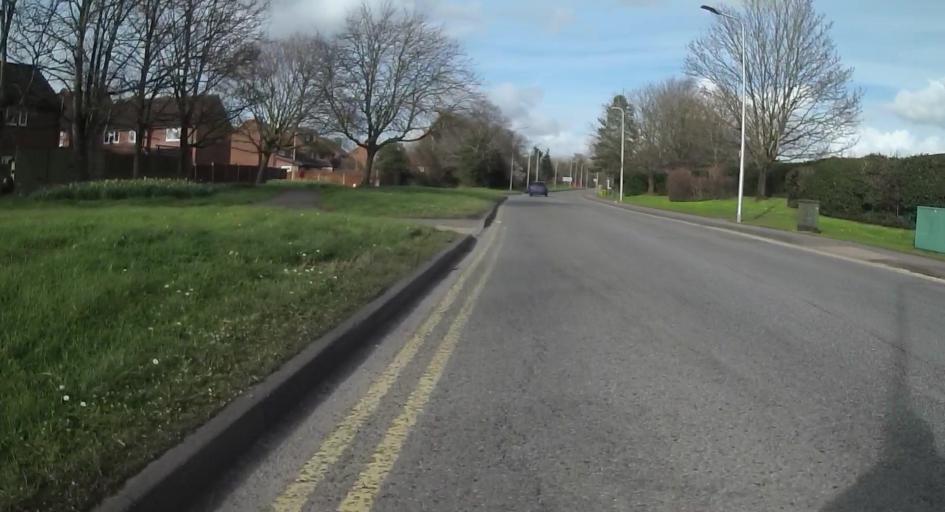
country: GB
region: England
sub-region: West Berkshire
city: Thatcham
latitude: 51.3997
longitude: -1.2376
